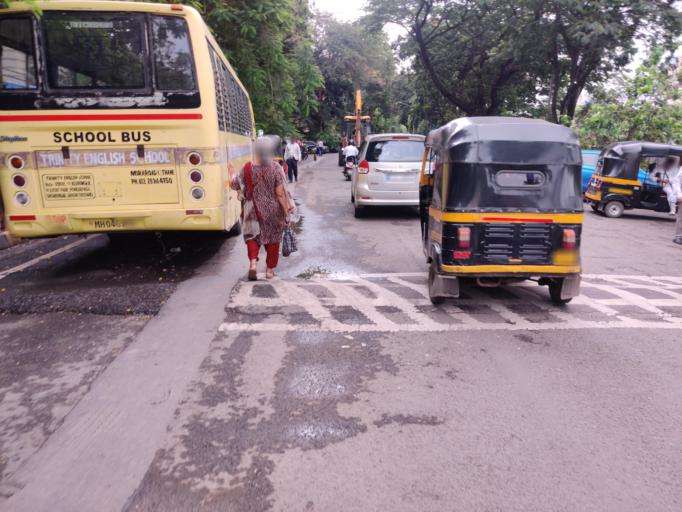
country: IN
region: Maharashtra
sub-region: Mumbai Suburban
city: Borivli
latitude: 19.2543
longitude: 72.8568
